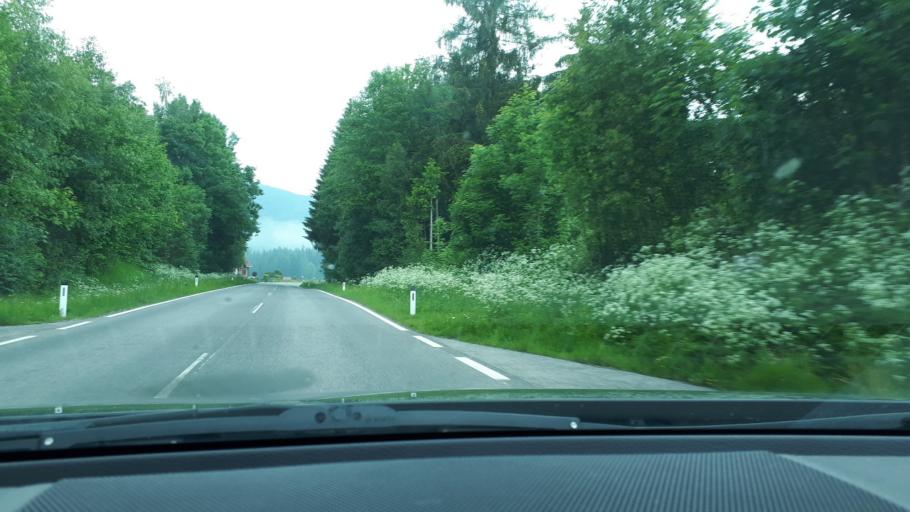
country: AT
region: Carinthia
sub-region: Politischer Bezirk Wolfsberg
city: Preitenegg
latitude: 46.9329
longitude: 14.9543
